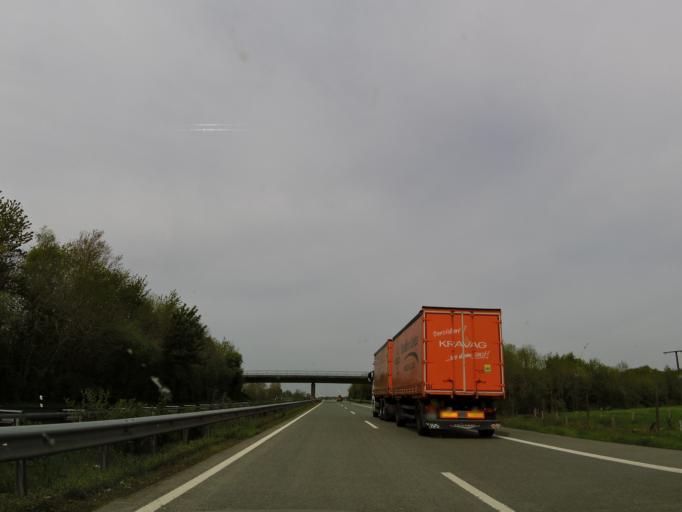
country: DE
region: Schleswig-Holstein
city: Nienbuttel
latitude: 54.0366
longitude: 9.4284
